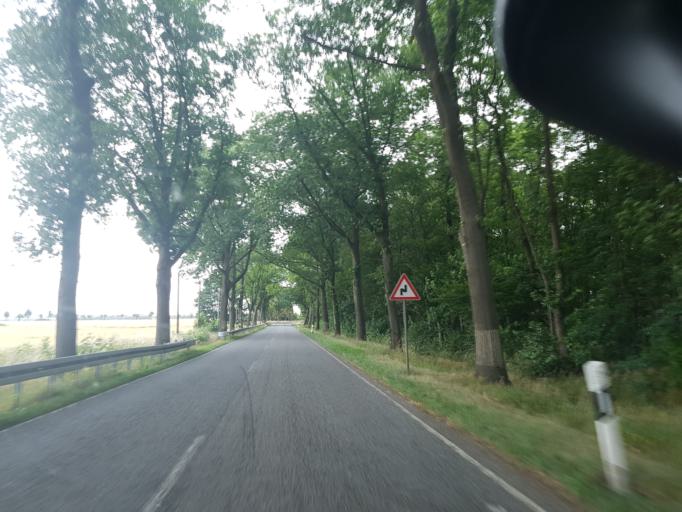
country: DE
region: Brandenburg
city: Dahme
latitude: 51.8501
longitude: 13.4106
